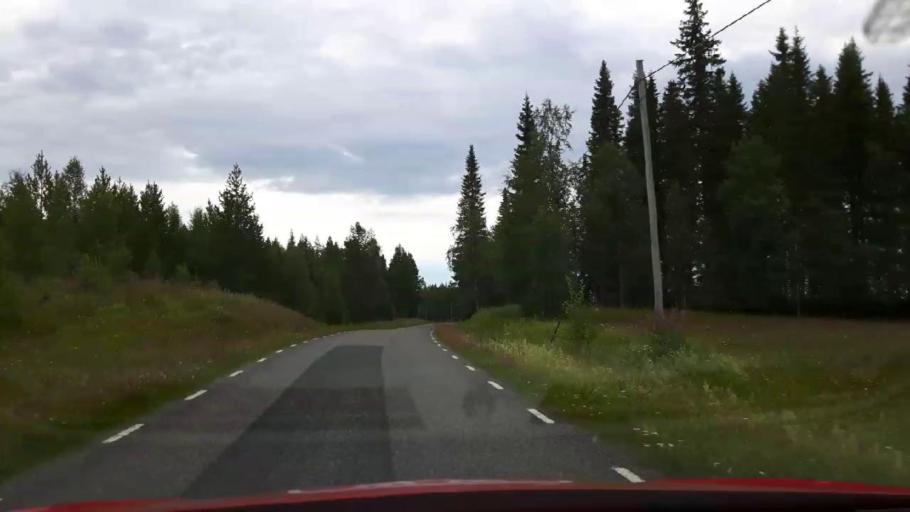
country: SE
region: Jaemtland
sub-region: OEstersunds Kommun
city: Lit
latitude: 63.3841
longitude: 15.0365
